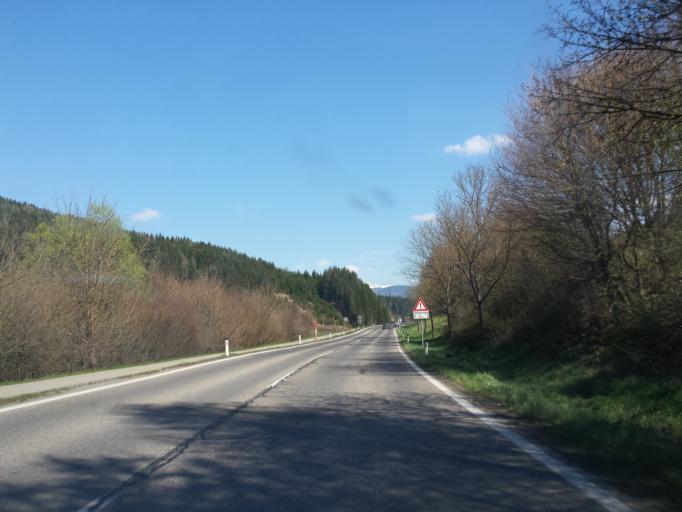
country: AT
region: Styria
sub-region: Politischer Bezirk Leoben
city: Traboch
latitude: 47.3809
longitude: 14.9872
